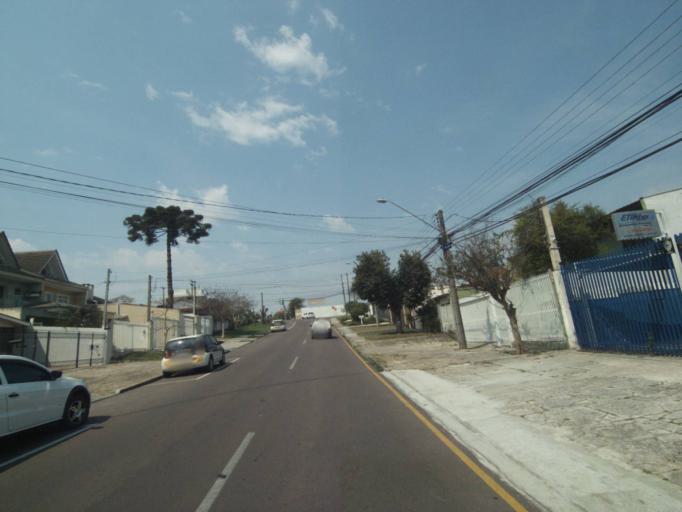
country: BR
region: Parana
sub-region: Curitiba
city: Curitiba
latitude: -25.4625
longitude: -49.2620
